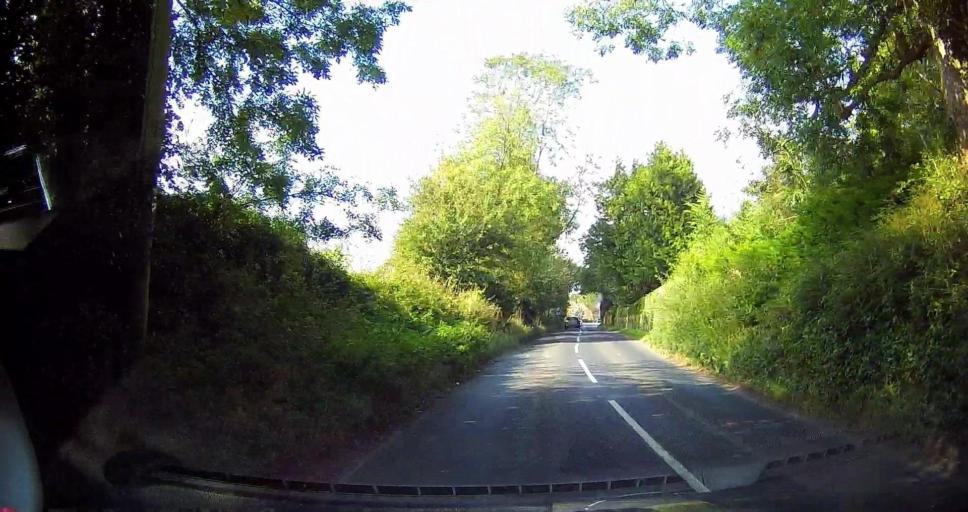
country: GB
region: England
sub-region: Kent
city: Wye
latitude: 51.1831
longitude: 0.9106
